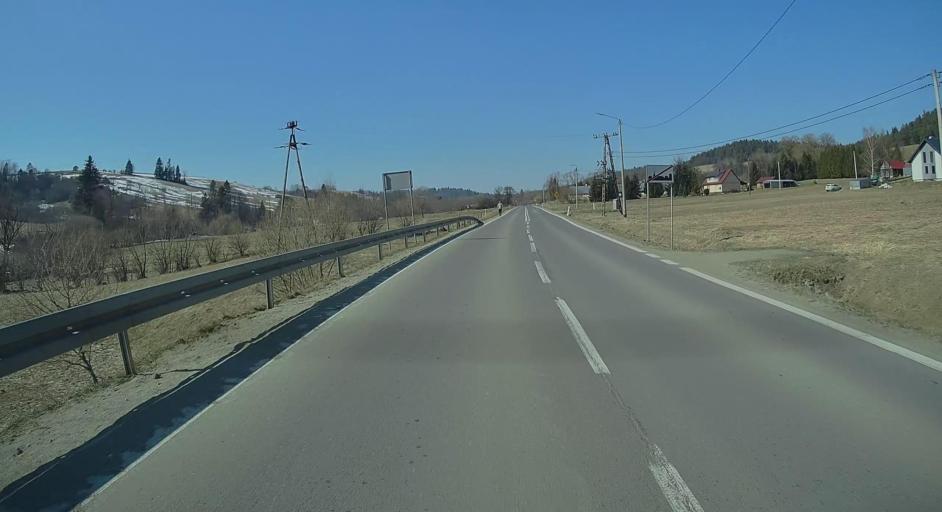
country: PL
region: Subcarpathian Voivodeship
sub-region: Powiat bieszczadzki
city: Ustrzyki Dolne
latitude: 49.5019
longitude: 22.6274
